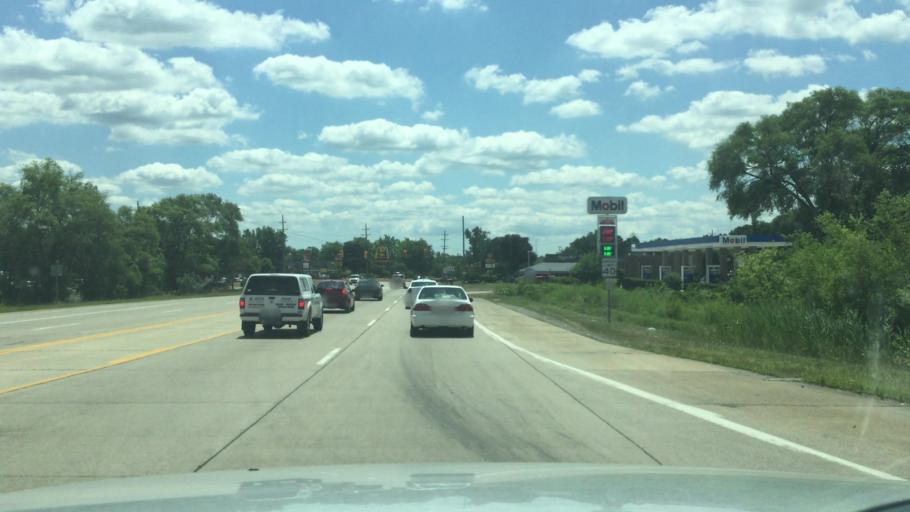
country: US
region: Michigan
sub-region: Wayne County
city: Belleville
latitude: 42.2167
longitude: -83.5450
